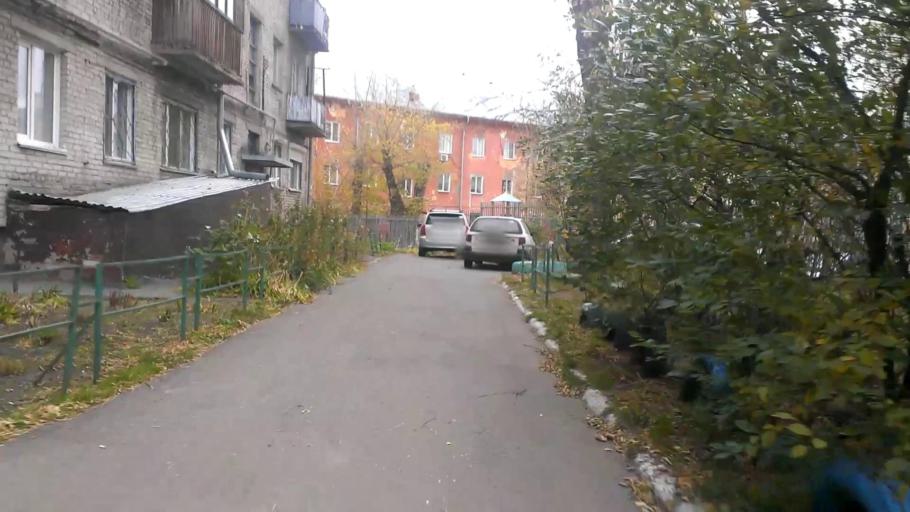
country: RU
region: Altai Krai
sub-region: Gorod Barnaulskiy
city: Barnaul
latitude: 53.3531
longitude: 83.7646
